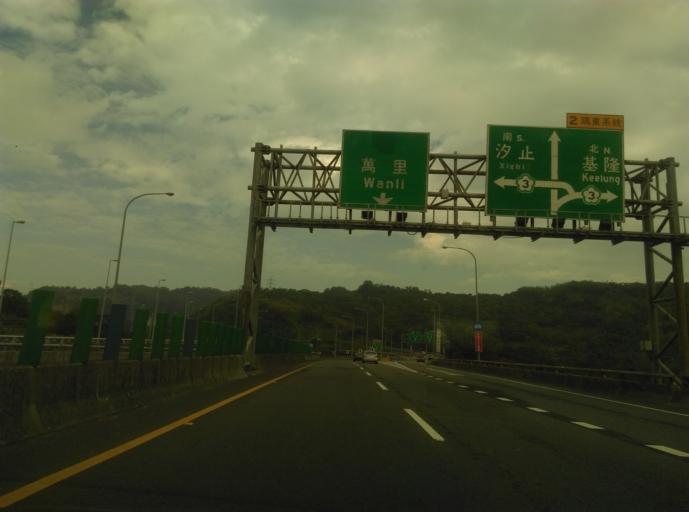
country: TW
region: Taiwan
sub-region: Keelung
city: Keelung
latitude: 25.1225
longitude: 121.6982
